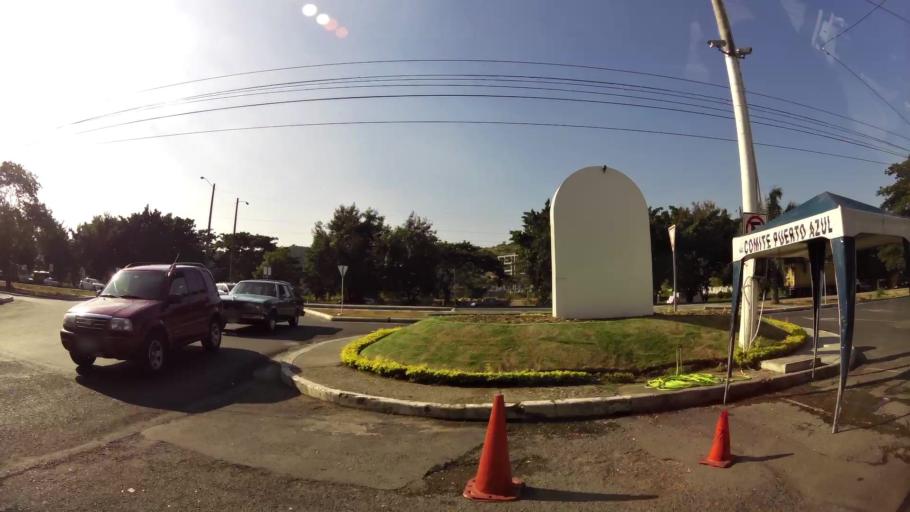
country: EC
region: Guayas
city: Santa Lucia
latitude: -2.1864
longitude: -79.9673
